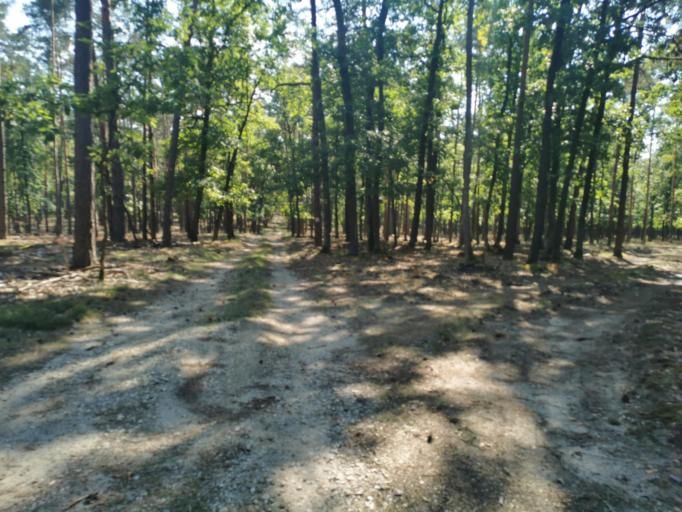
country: SK
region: Trnavsky
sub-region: Okres Senica
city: Senica
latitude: 48.6202
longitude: 17.2798
